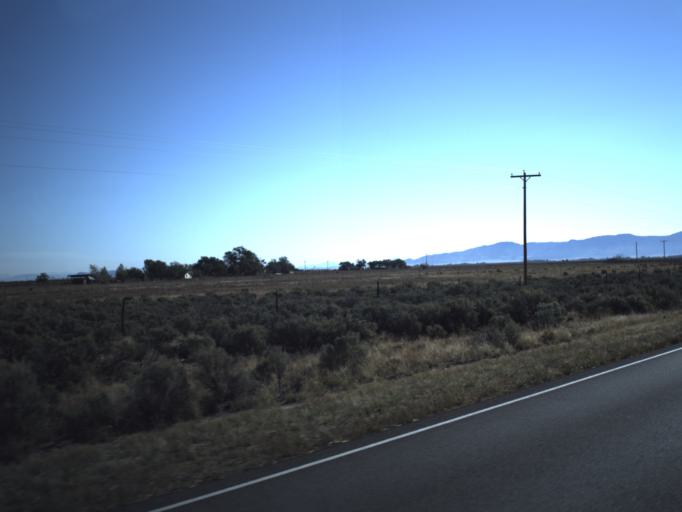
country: US
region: Utah
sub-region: Washington County
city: Enterprise
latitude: 37.7443
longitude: -113.7533
